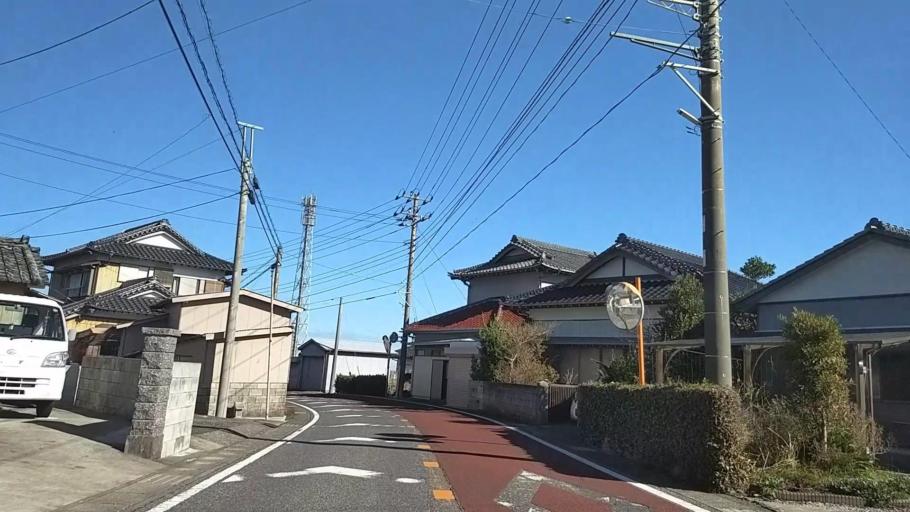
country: JP
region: Chiba
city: Tateyama
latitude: 34.9430
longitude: 139.9600
